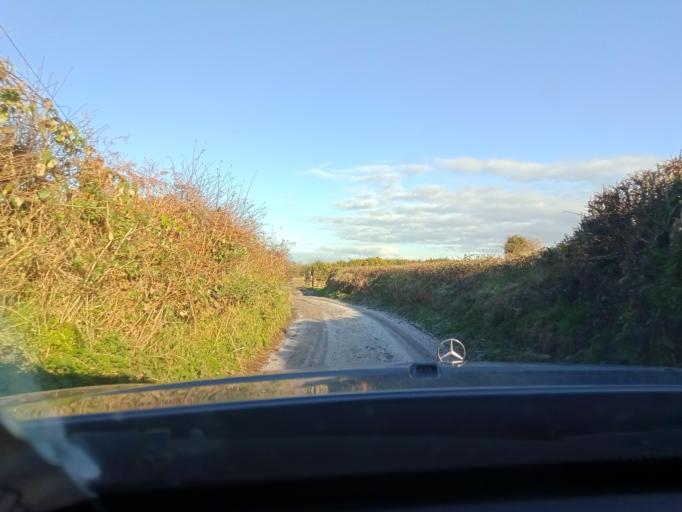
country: IE
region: Leinster
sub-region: Kilkenny
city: Graiguenamanagh
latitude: 52.5585
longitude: -6.9437
